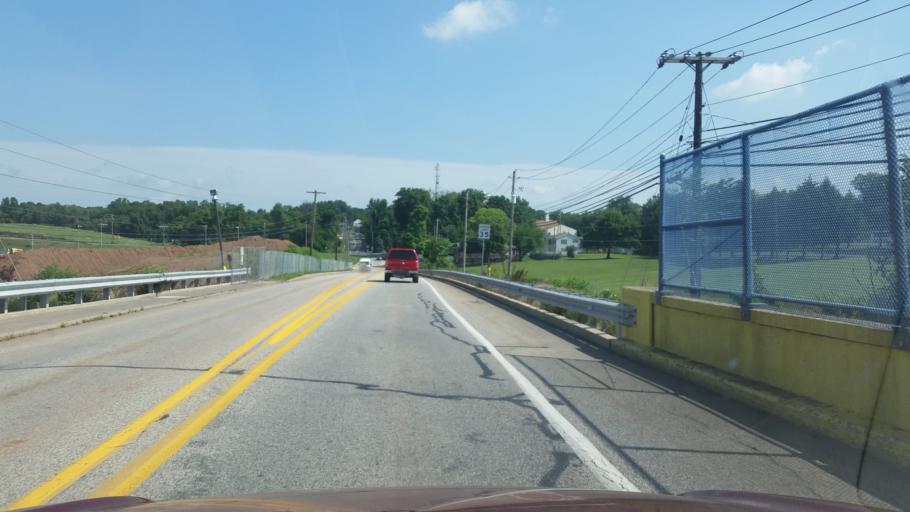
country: US
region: Pennsylvania
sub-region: Dauphin County
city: Middletown
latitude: 40.2102
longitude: -76.7359
